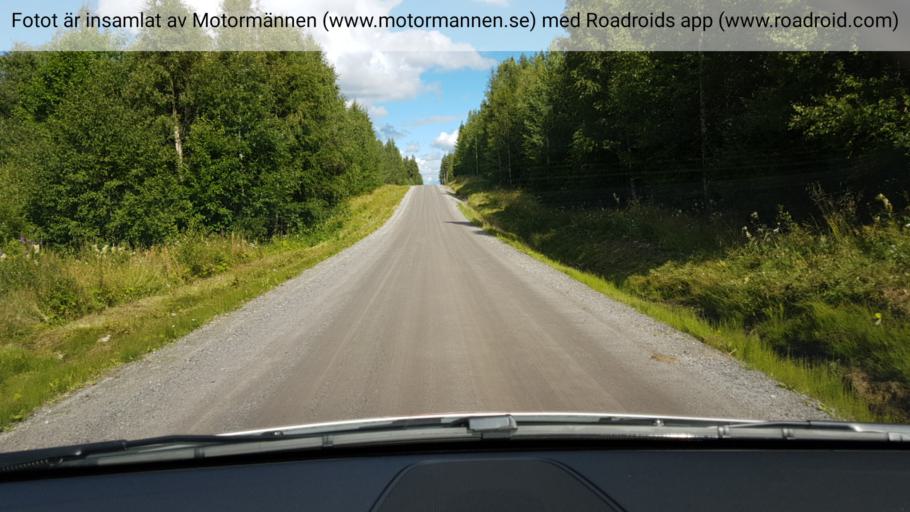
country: SE
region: Jaemtland
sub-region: Braecke Kommun
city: Braecke
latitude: 63.1206
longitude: 15.7520
